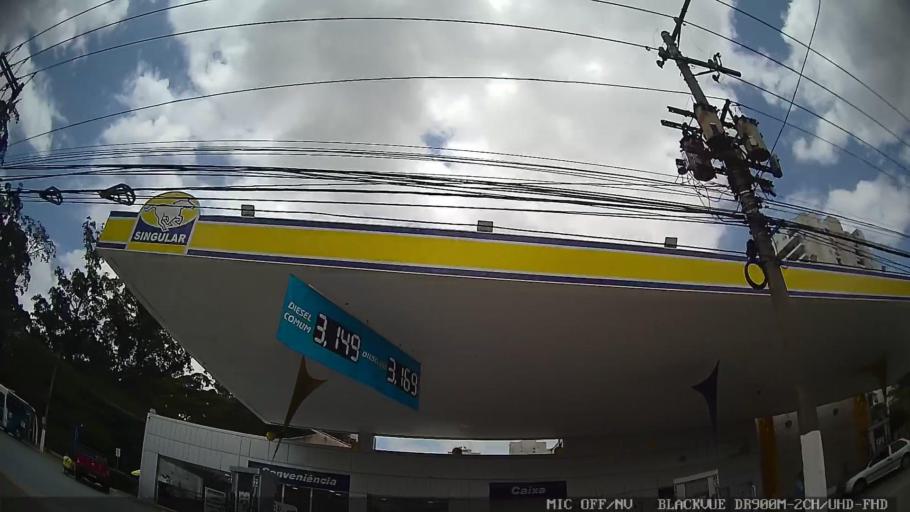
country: BR
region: Sao Paulo
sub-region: Sao Paulo
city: Sao Paulo
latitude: -23.5269
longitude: -46.5763
